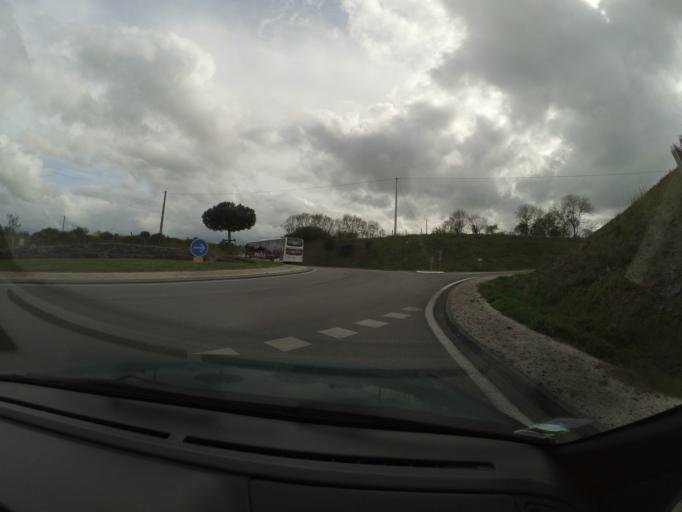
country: FR
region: Pays de la Loire
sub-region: Departement de Maine-et-Loire
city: Lire
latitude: 47.3306
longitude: -1.1678
